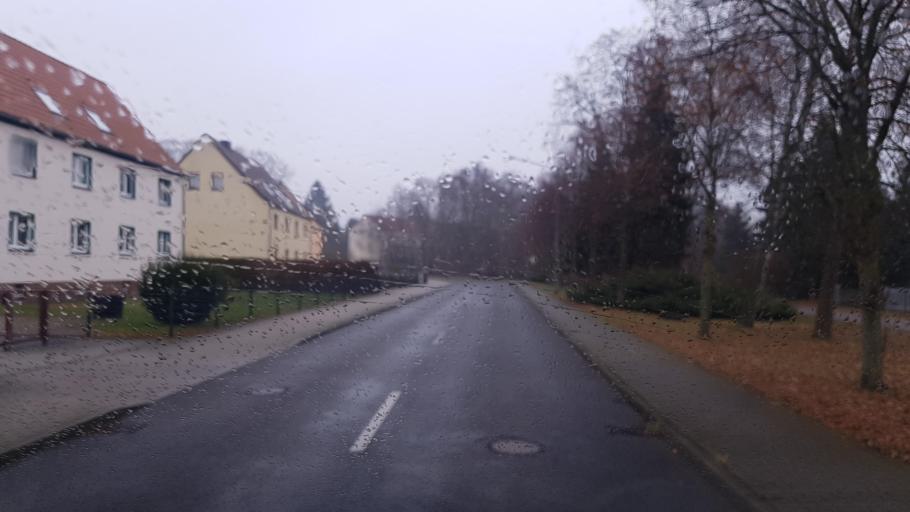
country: DE
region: Brandenburg
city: Lauchhammer
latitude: 51.4951
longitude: 13.7872
